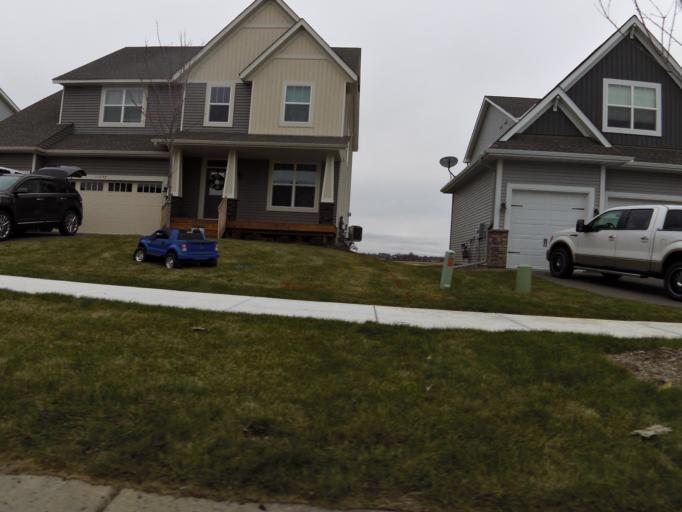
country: US
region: Minnesota
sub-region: Washington County
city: Lake Elmo
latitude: 44.9967
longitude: -92.8667
